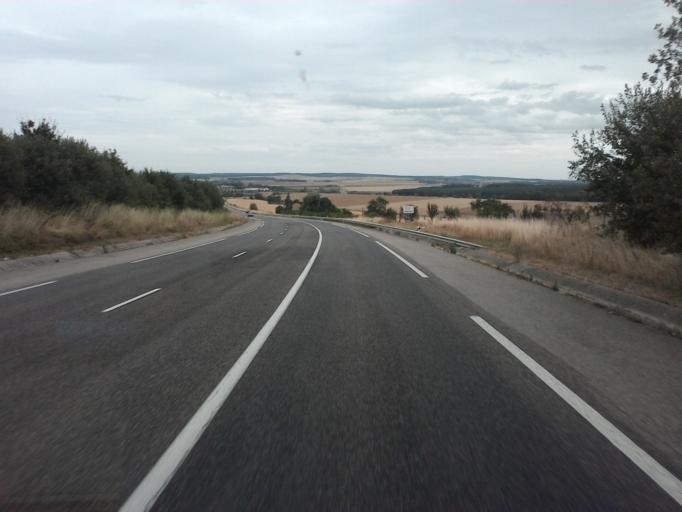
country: FR
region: Lorraine
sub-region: Departement de Meurthe-et-Moselle
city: Bainville-sur-Madon
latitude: 48.5791
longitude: 6.0328
